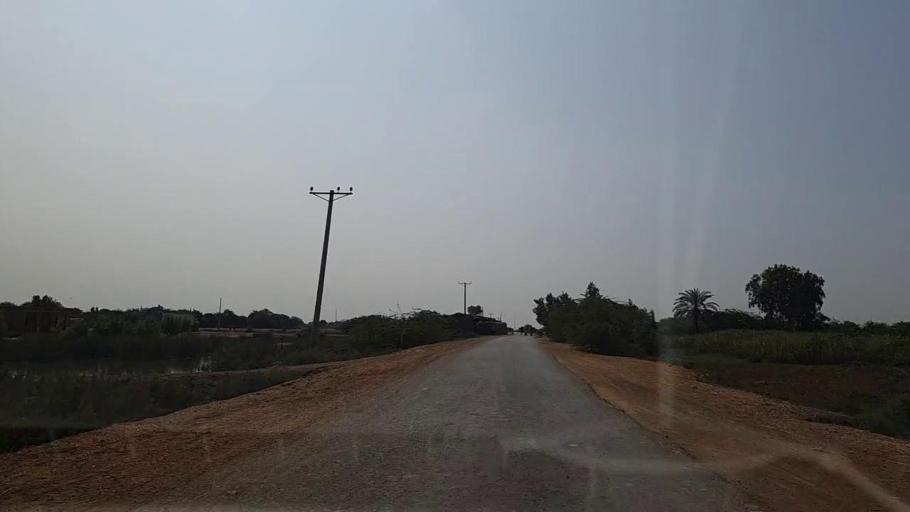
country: PK
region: Sindh
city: Chuhar Jamali
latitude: 24.3060
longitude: 67.9364
